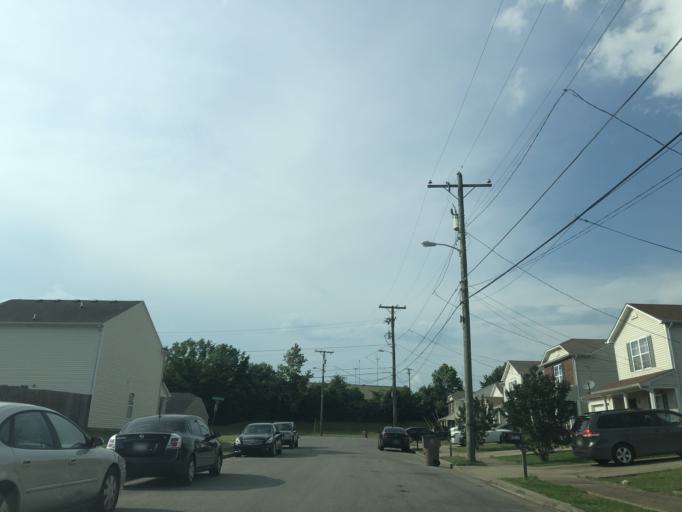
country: US
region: Tennessee
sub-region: Davidson County
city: Nashville
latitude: 36.2356
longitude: -86.7936
